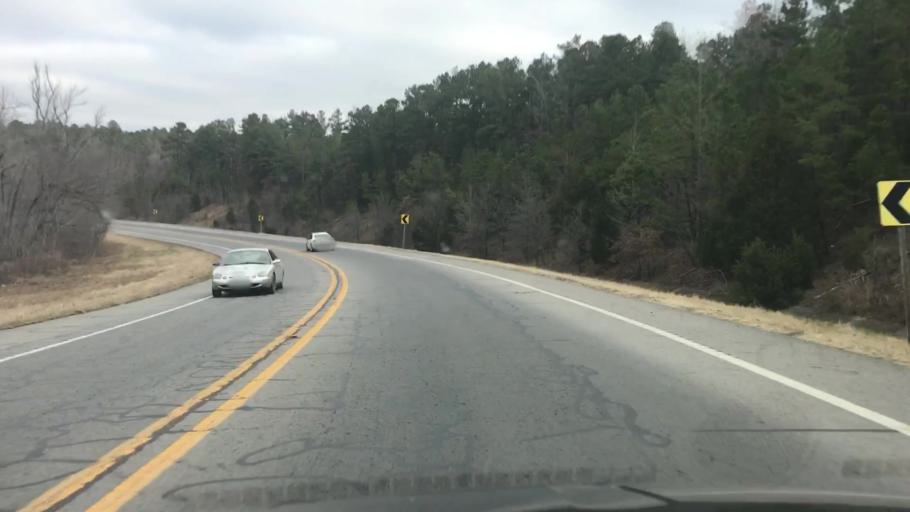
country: US
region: Arkansas
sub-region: Scott County
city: Waldron
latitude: 34.8219
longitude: -94.0364
